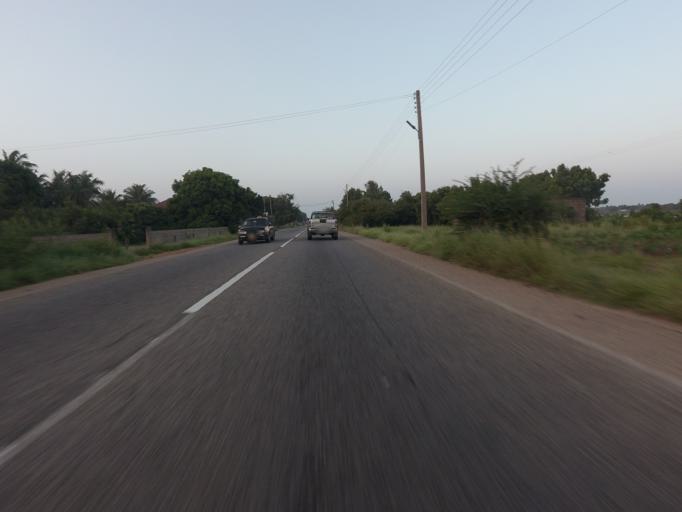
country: GH
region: Volta
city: Anloga
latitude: 5.8282
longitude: 0.9509
